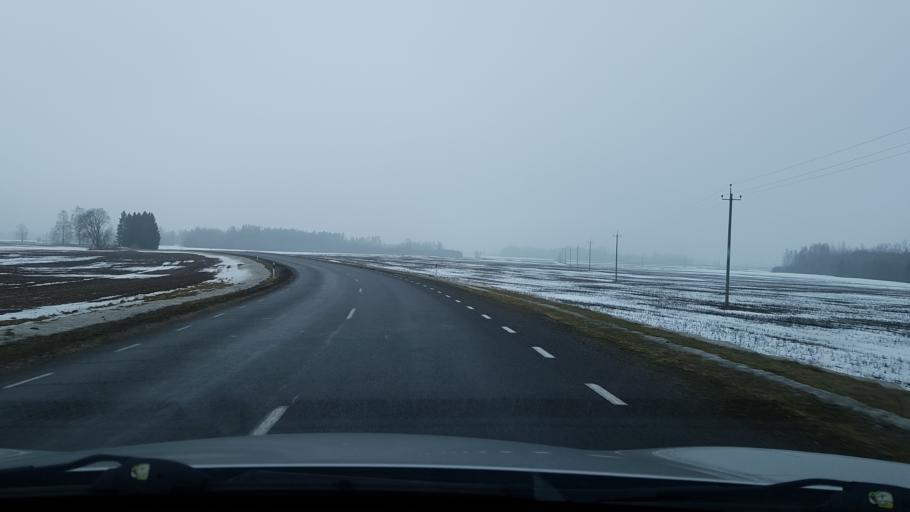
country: EE
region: Valgamaa
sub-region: Torva linn
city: Torva
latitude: 58.0940
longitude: 26.0106
